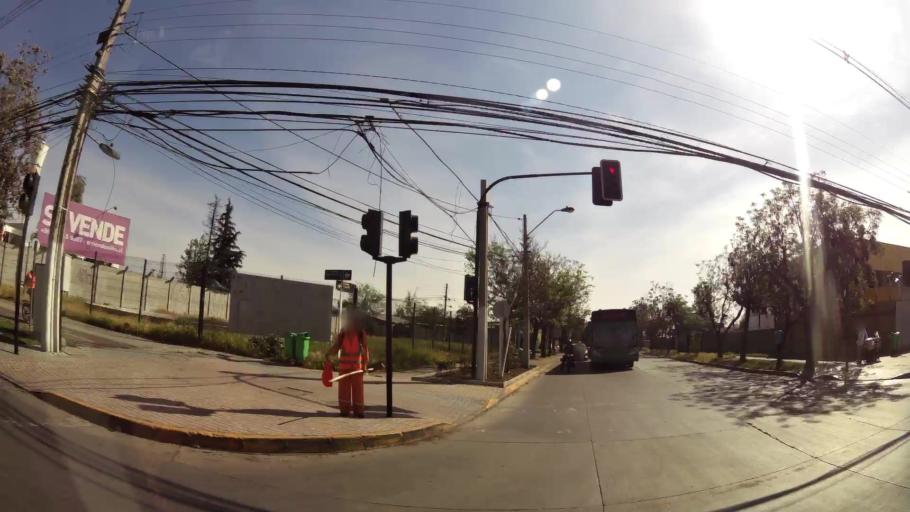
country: CL
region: Santiago Metropolitan
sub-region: Provincia de Santiago
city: La Pintana
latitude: -33.5286
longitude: -70.5961
